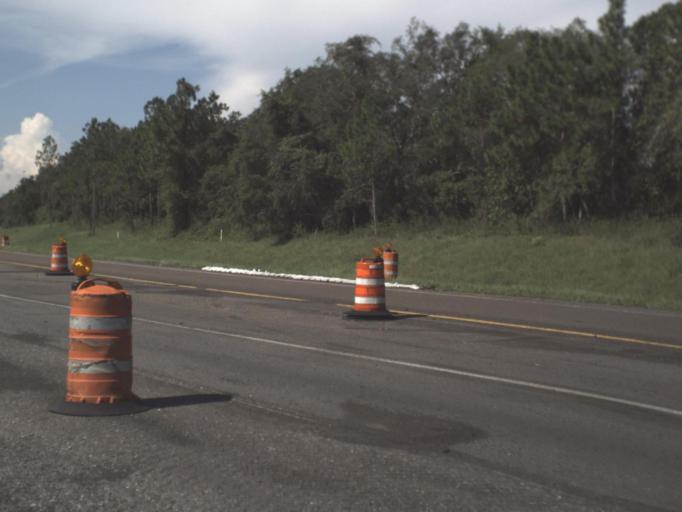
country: US
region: Florida
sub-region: Hillsborough County
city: Temple Terrace
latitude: 28.0754
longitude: -82.3540
